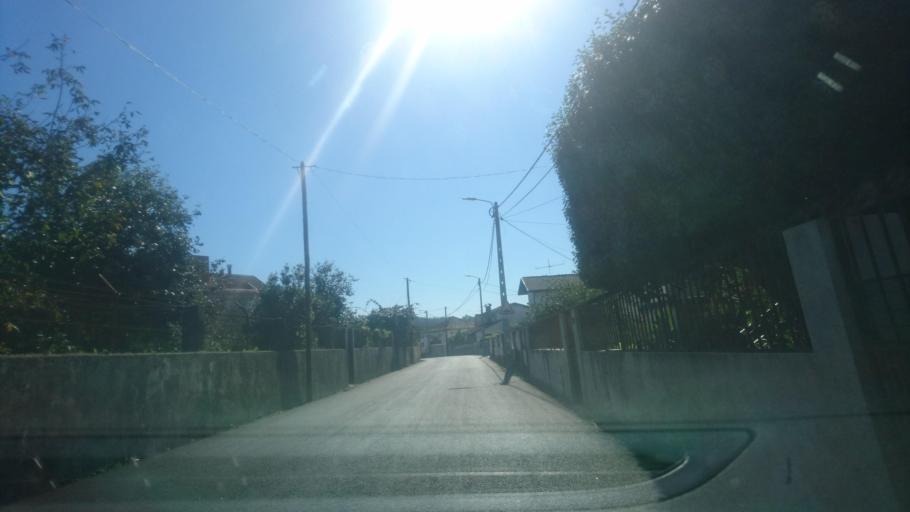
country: PT
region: Aveiro
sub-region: Santa Maria da Feira
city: Lamas
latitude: 40.9862
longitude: -8.5717
